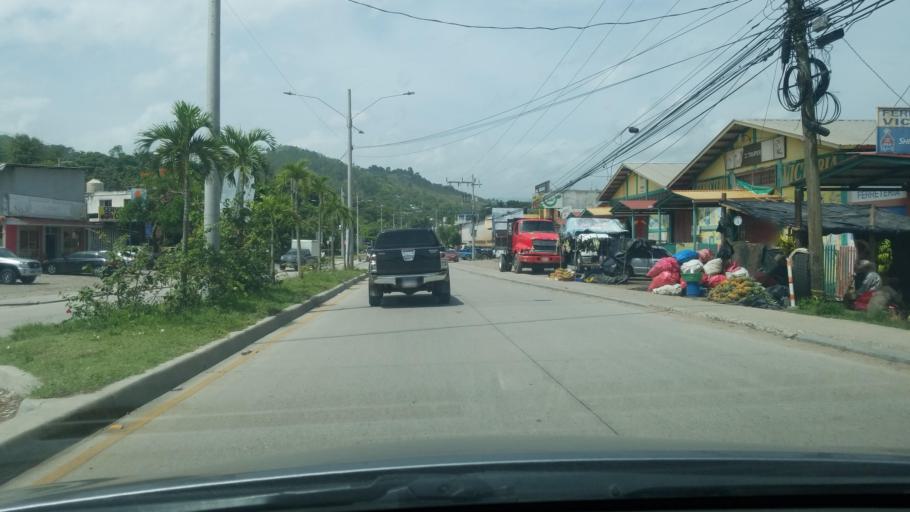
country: HN
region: Copan
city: La Entrada
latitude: 15.0569
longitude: -88.7549
